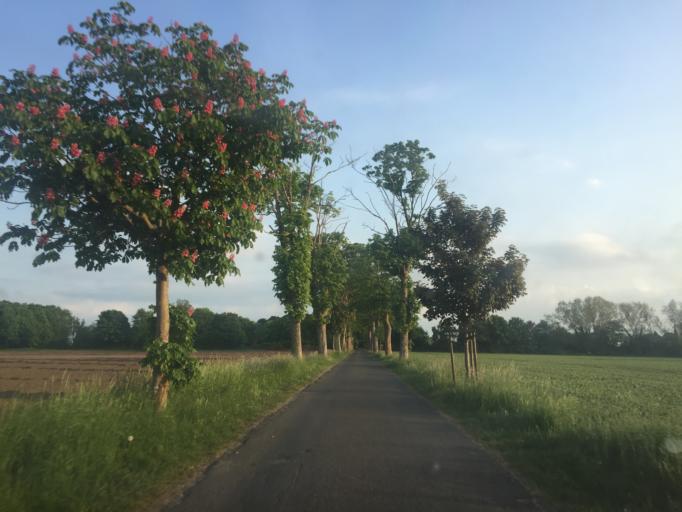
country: DK
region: South Denmark
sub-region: Kerteminde Kommune
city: Langeskov
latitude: 55.3495
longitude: 10.5242
